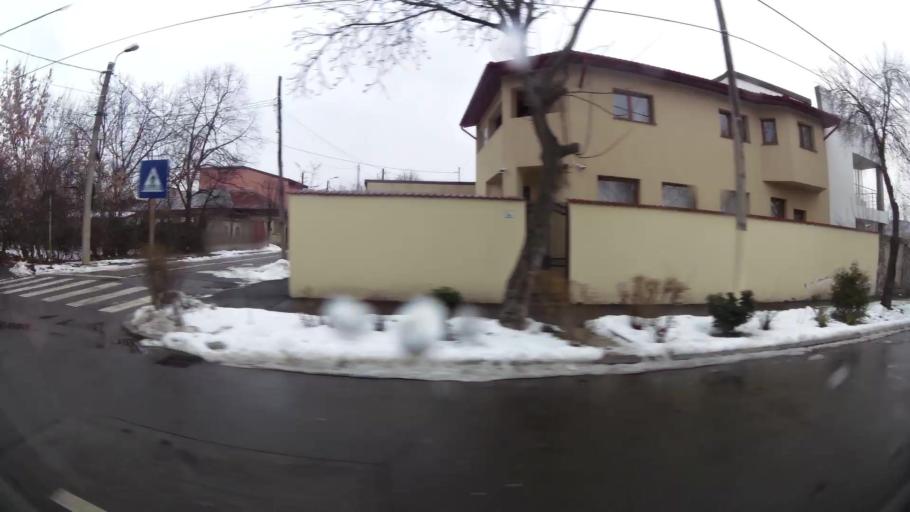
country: RO
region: Ilfov
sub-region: Comuna Chiajna
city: Rosu
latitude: 44.4888
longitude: 26.0216
